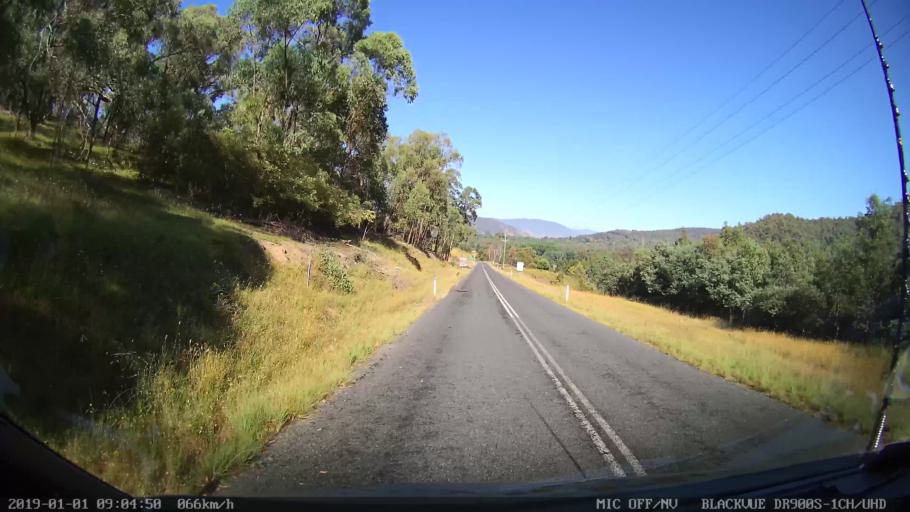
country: AU
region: New South Wales
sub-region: Snowy River
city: Jindabyne
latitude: -36.2212
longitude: 148.1521
